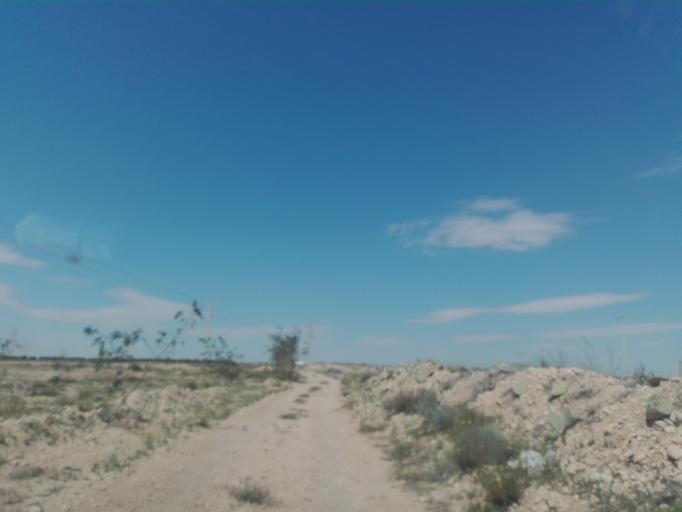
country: TN
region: Safaqis
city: Sfax
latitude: 34.6879
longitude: 10.5395
